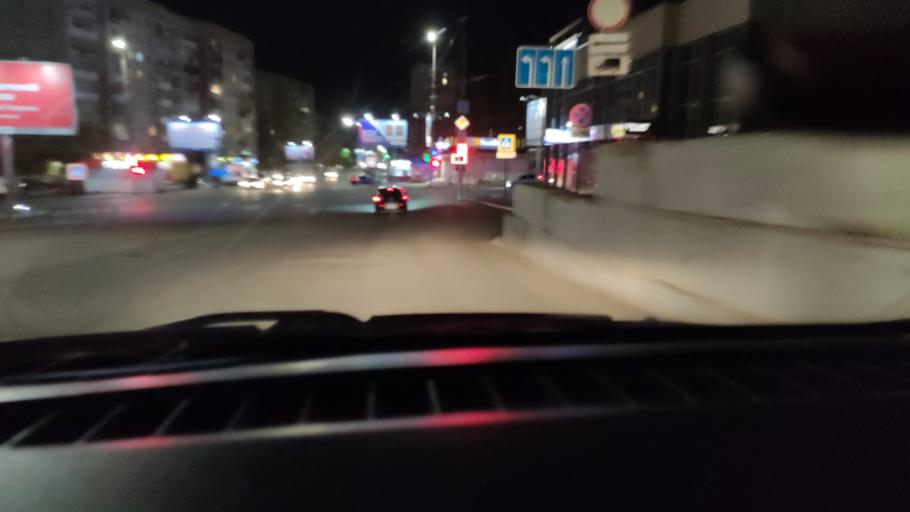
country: RU
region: Saratov
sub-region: Saratovskiy Rayon
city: Saratov
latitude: 51.5644
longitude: 46.0213
